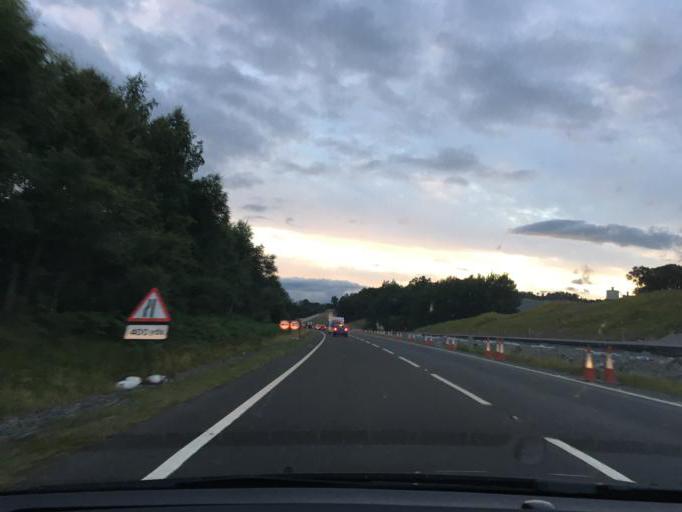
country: GB
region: Scotland
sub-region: Highland
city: Kingussie
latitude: 57.1130
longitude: -3.9549
